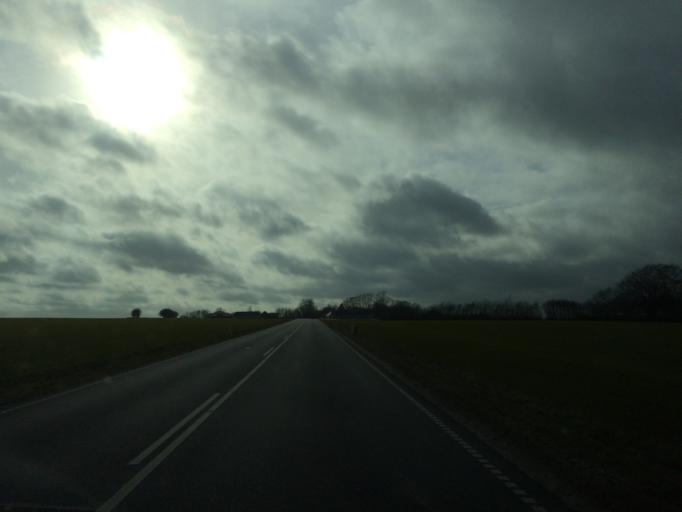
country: DK
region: Central Jutland
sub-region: Favrskov Kommune
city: Ulstrup
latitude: 56.4956
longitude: 9.8248
